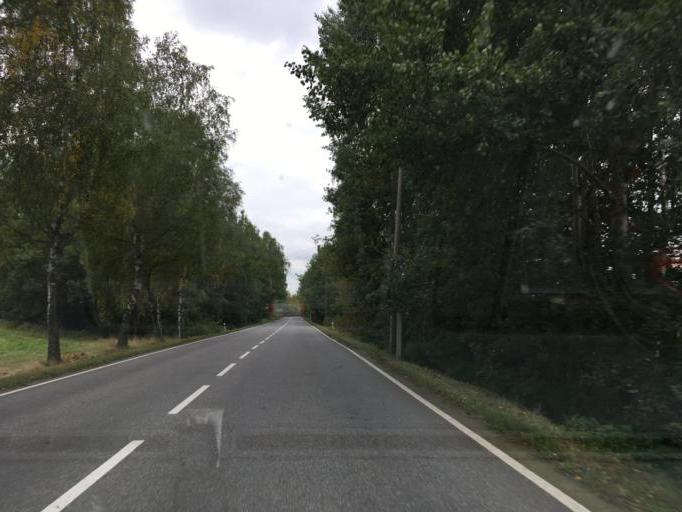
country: CZ
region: Vysocina
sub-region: Okres Pelhrimov
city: Pelhrimov
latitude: 49.4633
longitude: 15.1852
